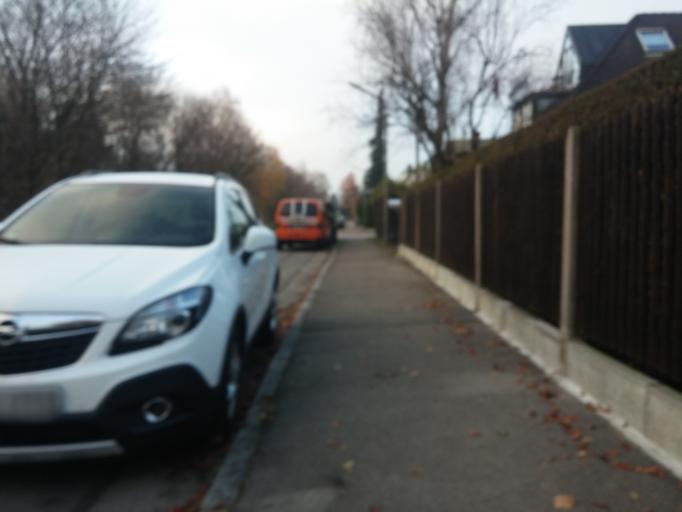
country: DE
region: Bavaria
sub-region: Upper Bavaria
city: Haar
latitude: 48.1027
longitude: 11.7059
